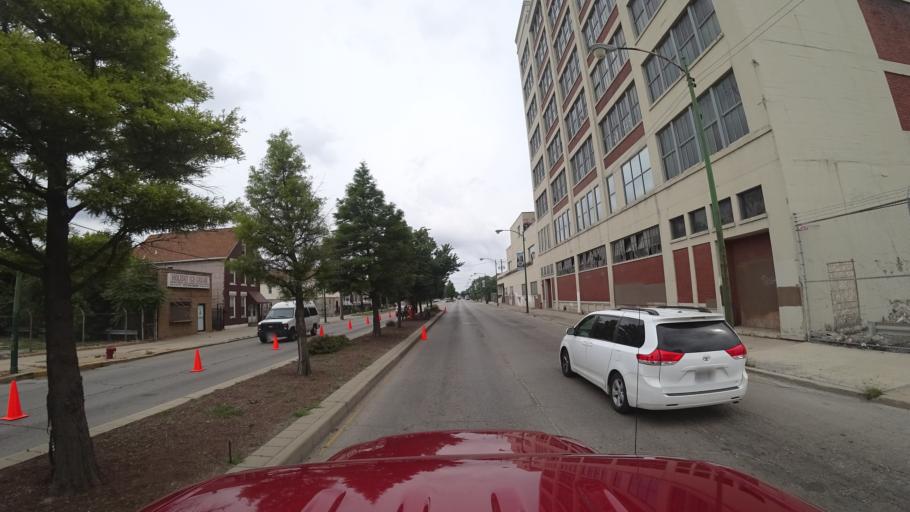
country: US
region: Illinois
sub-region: Cook County
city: Chicago
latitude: 41.8277
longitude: -87.6654
